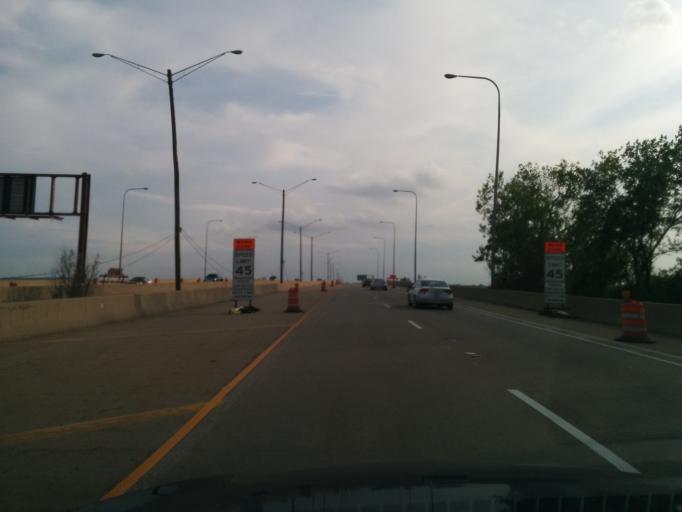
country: US
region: Illinois
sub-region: DuPage County
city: Hanover Park
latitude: 41.9910
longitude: -88.1252
